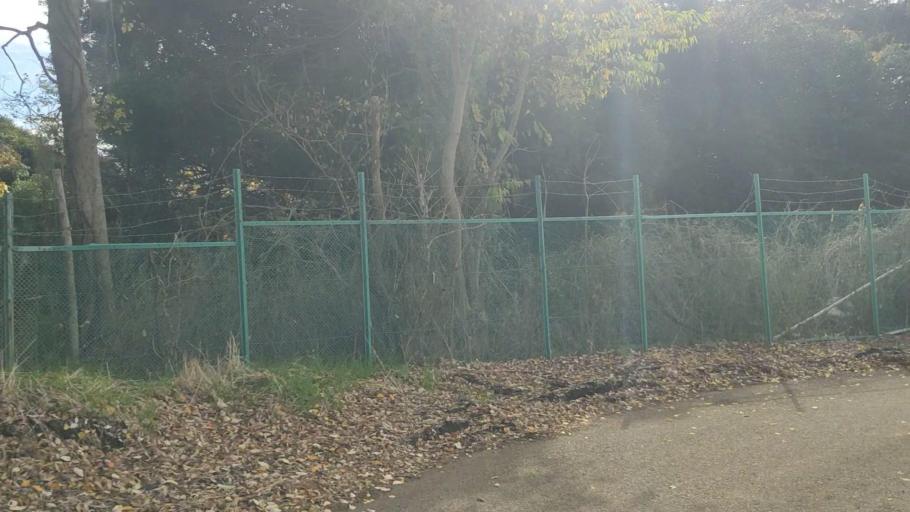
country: JP
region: Kanagawa
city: Minami-rinkan
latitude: 35.4867
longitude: 139.4983
